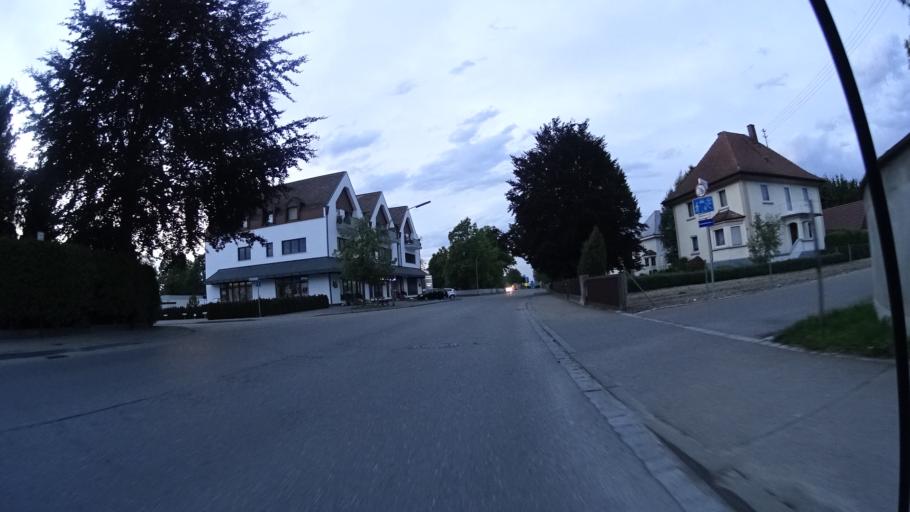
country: DE
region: Bavaria
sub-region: Swabia
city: Pfaffenhofen an der Roth
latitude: 48.3566
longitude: 10.1601
